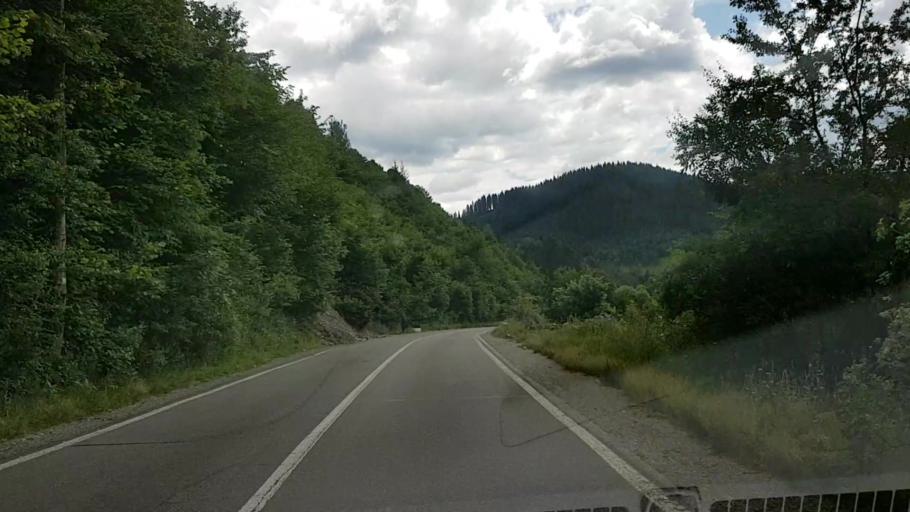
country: RO
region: Suceava
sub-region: Comuna Brosteni
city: Brosteni
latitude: 47.2352
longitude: 25.7428
